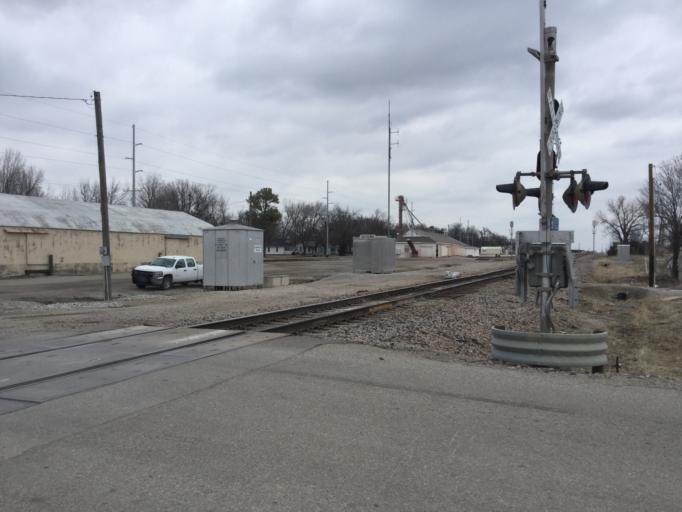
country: US
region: Kansas
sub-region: Cherokee County
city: Columbus
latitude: 37.1634
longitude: -94.8381
